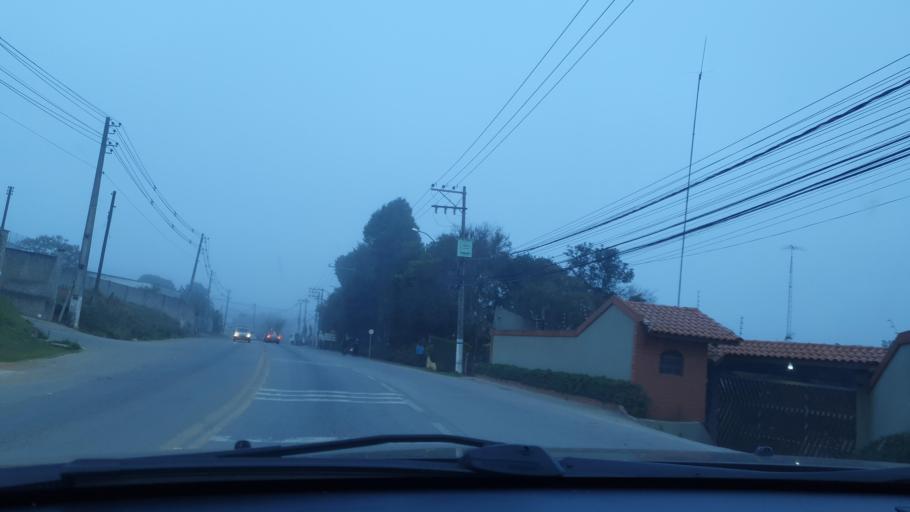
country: BR
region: Sao Paulo
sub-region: Ibiuna
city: Ibiuna
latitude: -23.6630
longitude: -47.2267
